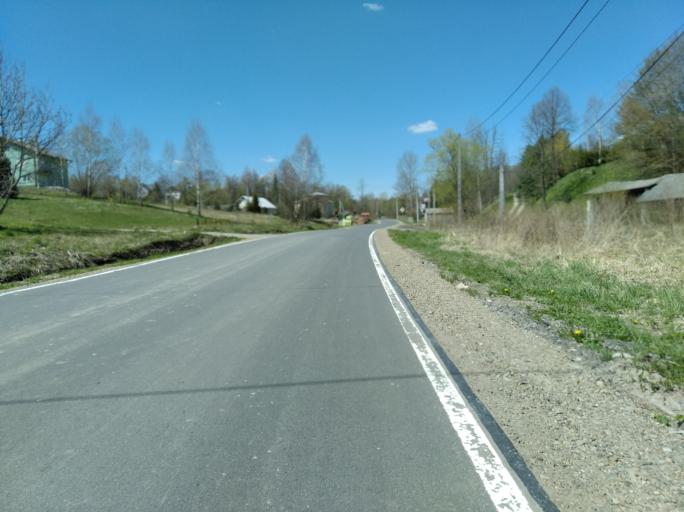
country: PL
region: Subcarpathian Voivodeship
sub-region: Powiat brzozowski
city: Jablonka
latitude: 49.7177
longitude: 22.1267
